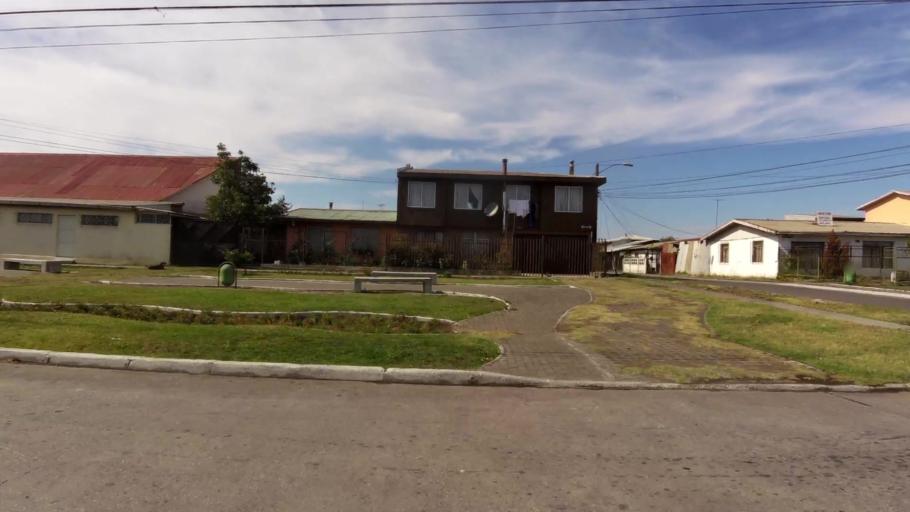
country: CL
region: Biobio
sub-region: Provincia de Concepcion
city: Talcahuano
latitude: -36.7781
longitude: -73.1103
